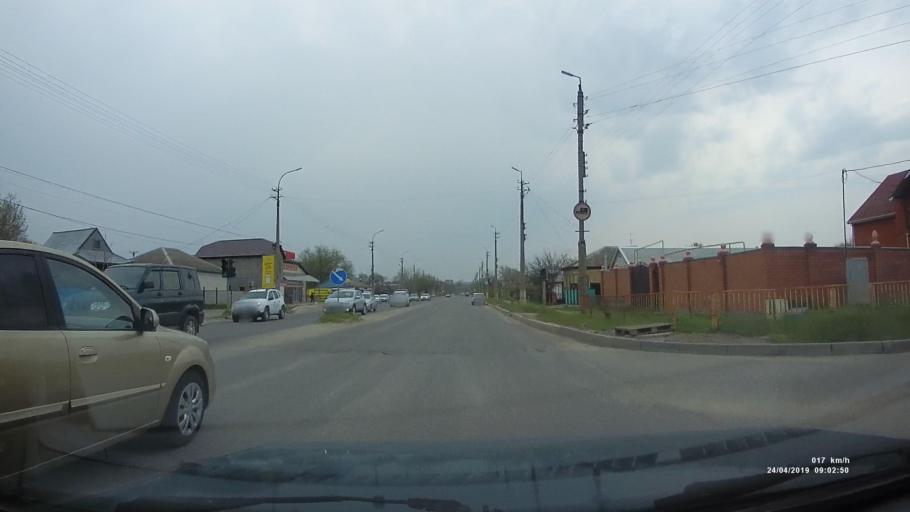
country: RU
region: Kalmykiya
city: Elista
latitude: 46.3119
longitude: 44.2335
